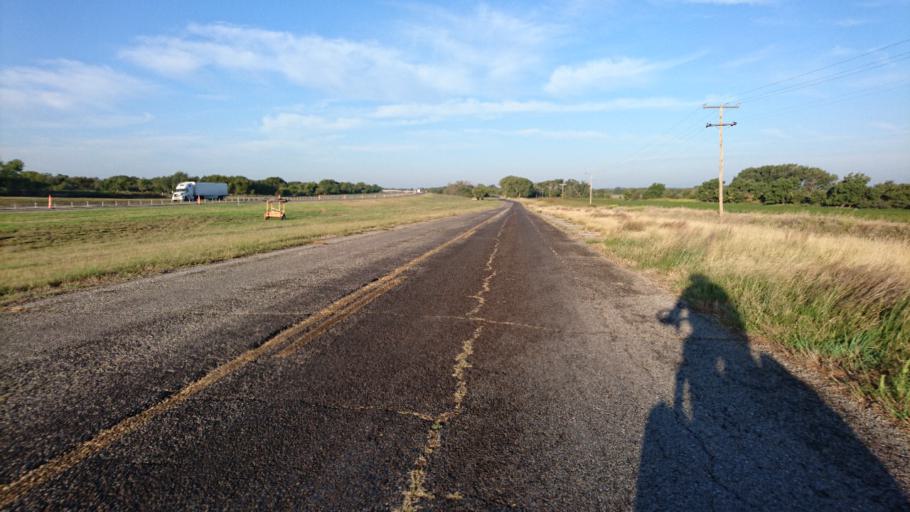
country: US
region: Oklahoma
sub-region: Beckham County
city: Sayre
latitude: 35.2625
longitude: -99.7040
